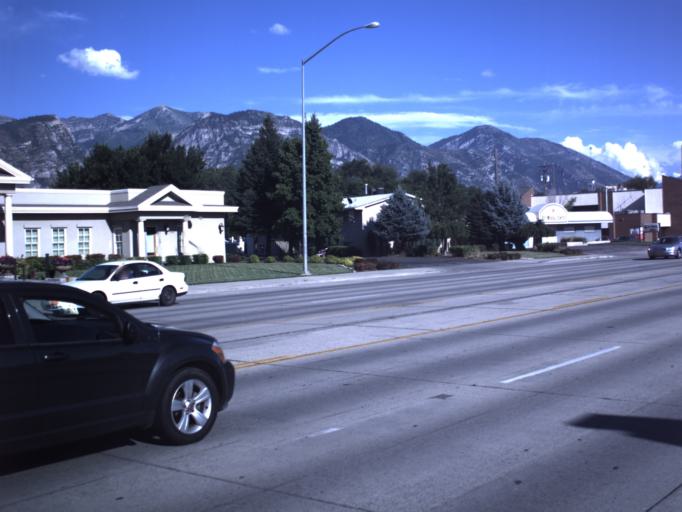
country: US
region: Utah
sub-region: Utah County
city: Orem
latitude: 40.2882
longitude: -111.6912
